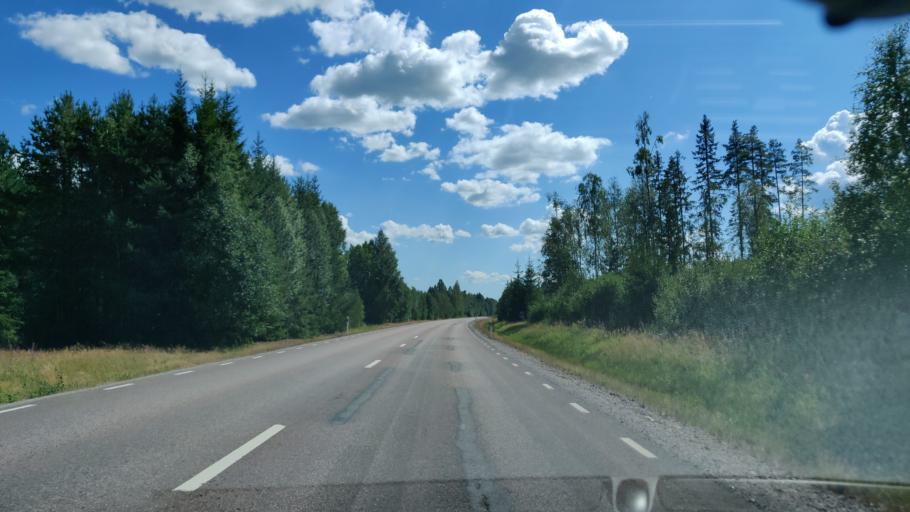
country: SE
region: Vaermland
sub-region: Hagfors Kommun
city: Ekshaerad
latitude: 60.2054
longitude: 13.4908
